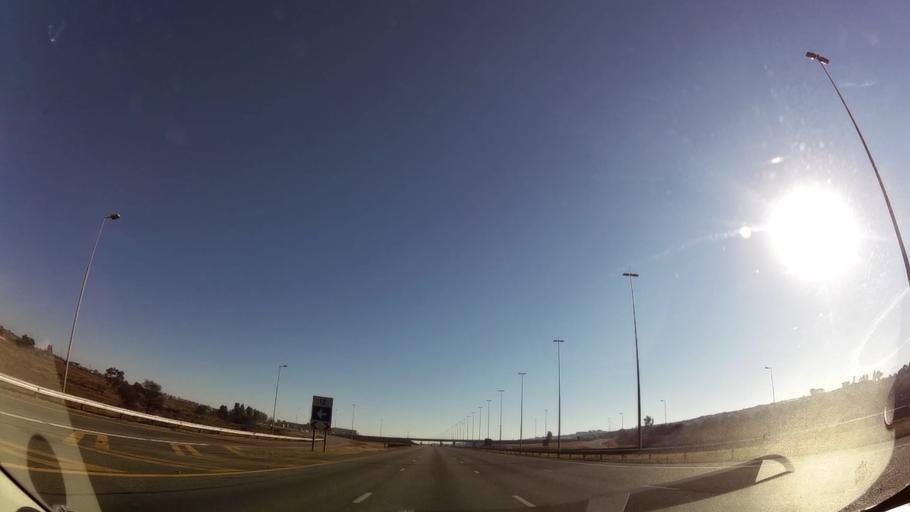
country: ZA
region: Gauteng
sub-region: City of Tshwane Metropolitan Municipality
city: Centurion
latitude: -25.8694
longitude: 28.2540
